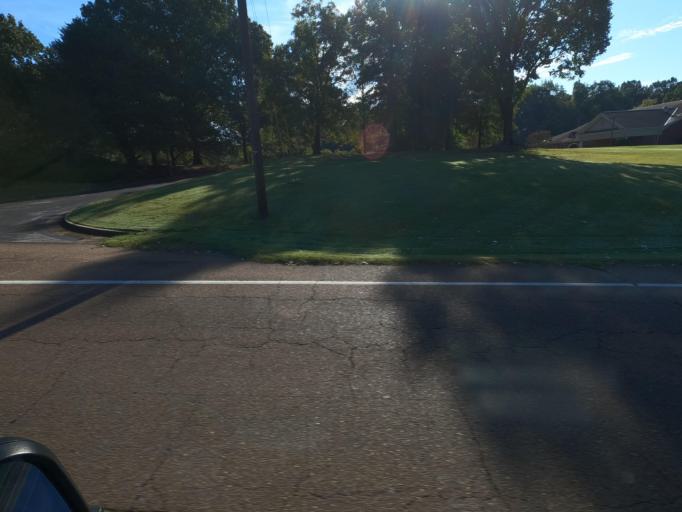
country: US
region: Tennessee
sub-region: Shelby County
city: Millington
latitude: 35.3889
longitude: -89.8563
